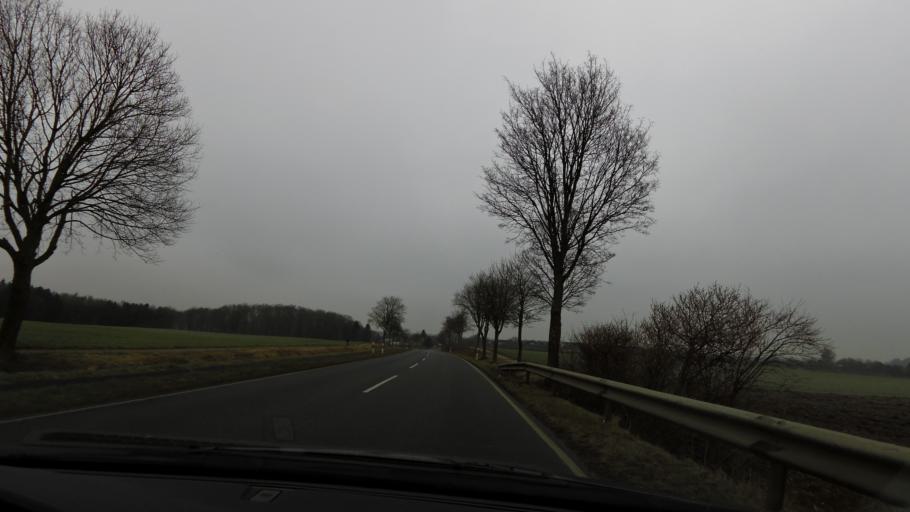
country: DE
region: North Rhine-Westphalia
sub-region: Regierungsbezirk Koln
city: Ubach-Palenberg
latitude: 50.9125
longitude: 6.1021
